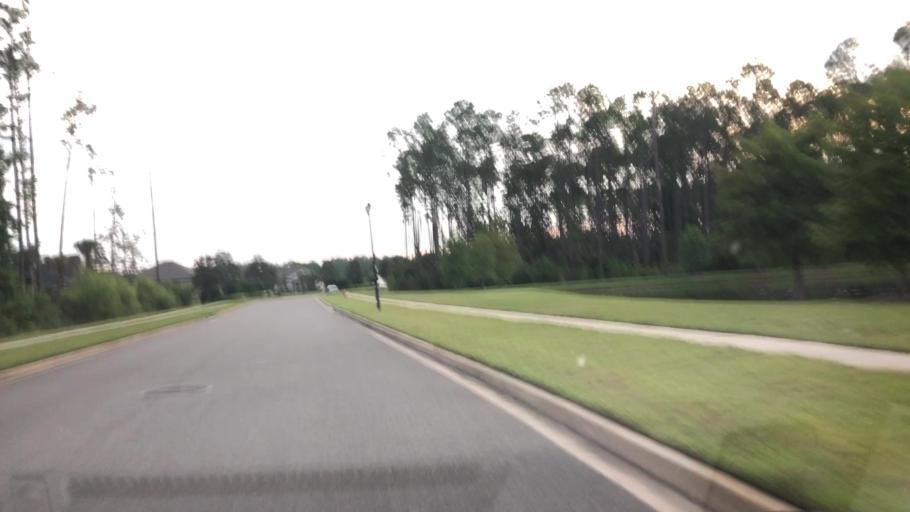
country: US
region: Florida
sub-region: Saint Johns County
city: Palm Valley
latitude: 30.1158
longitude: -81.4523
